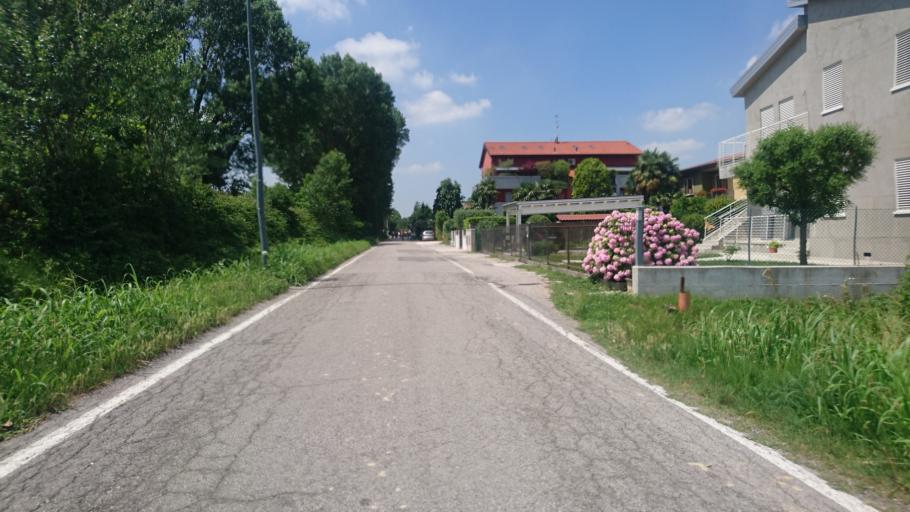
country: IT
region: Veneto
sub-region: Provincia di Venezia
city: Fiesso
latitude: 45.4153
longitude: 12.0478
